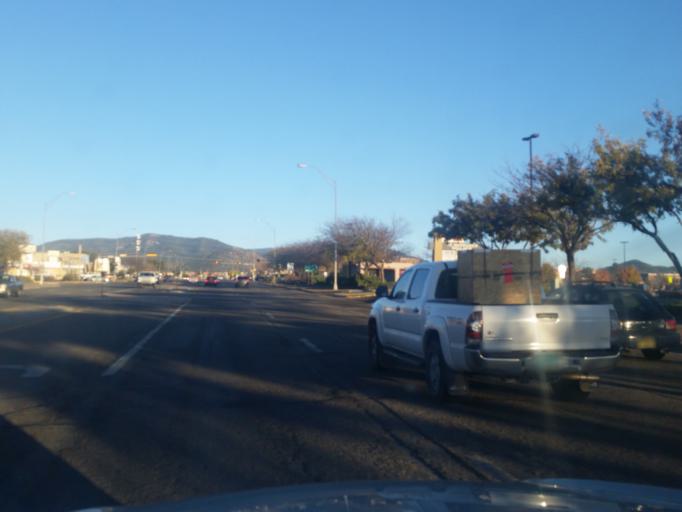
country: US
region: New Mexico
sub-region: Santa Fe County
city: Santa Fe
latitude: 35.6592
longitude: -105.9716
